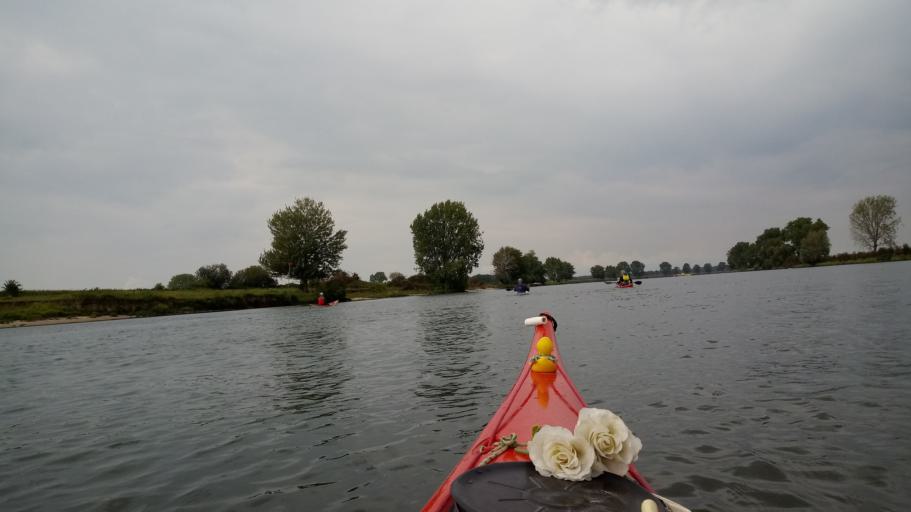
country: NL
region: Gelderland
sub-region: Gemeente Maasdriel
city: Heerewaarden
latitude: 51.7710
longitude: 5.3601
